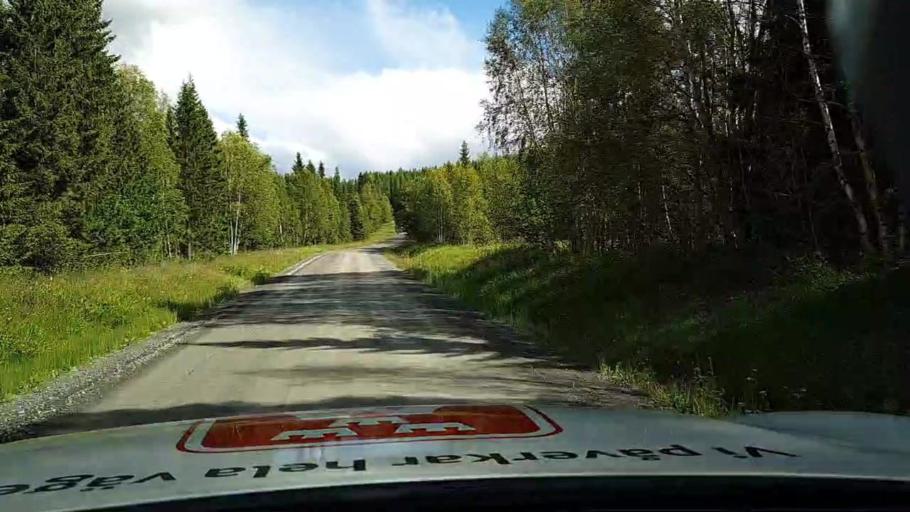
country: SE
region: Jaemtland
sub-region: Krokoms Kommun
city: Valla
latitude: 63.6768
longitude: 13.6866
